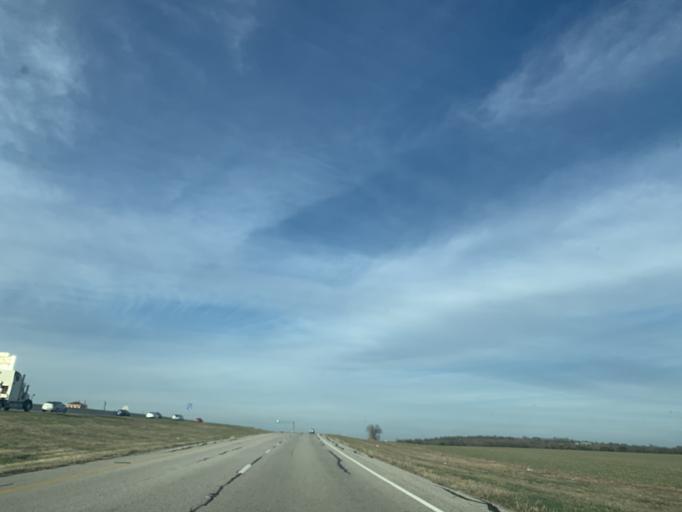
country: US
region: Texas
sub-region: Bell County
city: Salado
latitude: 30.8790
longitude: -97.5785
